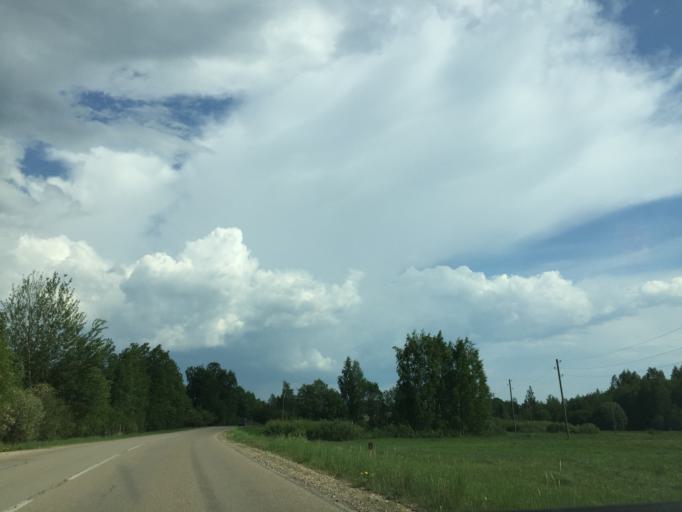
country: LV
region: Rezekne
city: Rezekne
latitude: 56.4777
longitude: 27.3646
